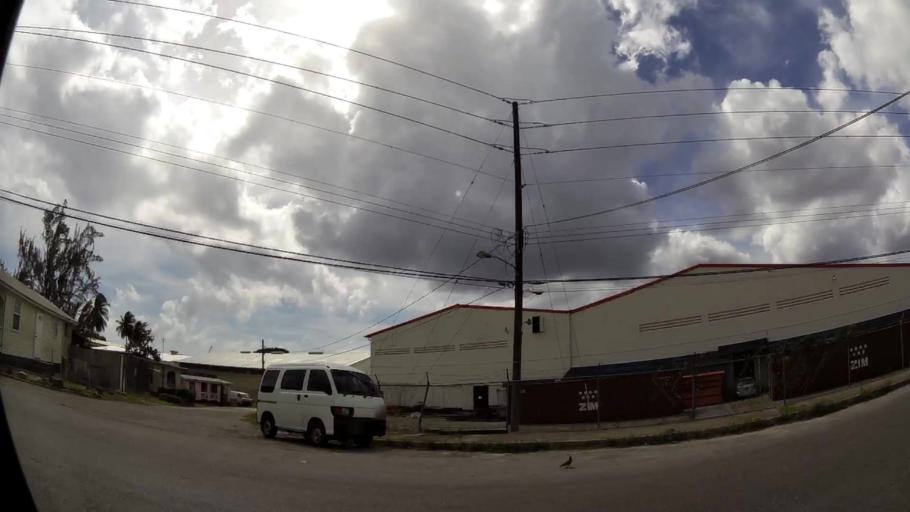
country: BB
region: Saint Michael
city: Bridgetown
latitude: 13.1117
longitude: -59.6251
